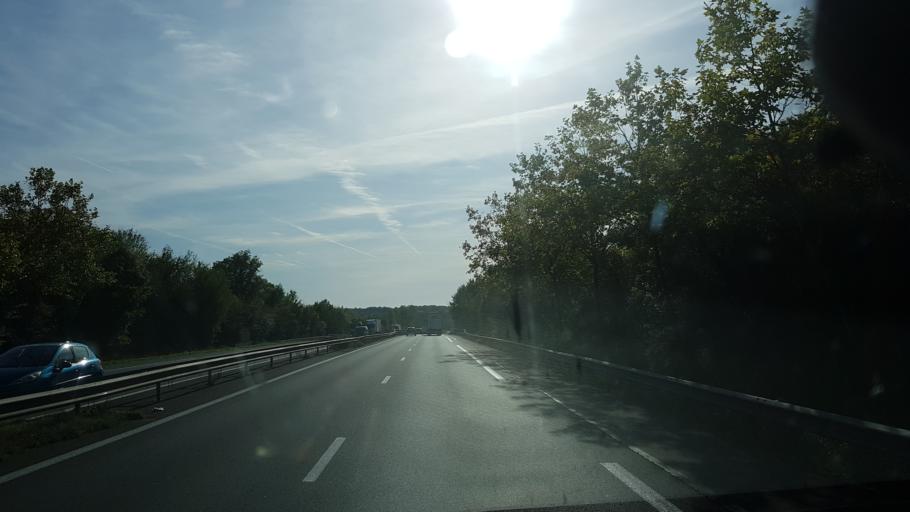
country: FR
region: Poitou-Charentes
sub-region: Departement de la Charente
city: Gond-Pontouvre
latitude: 45.6894
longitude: 0.1592
